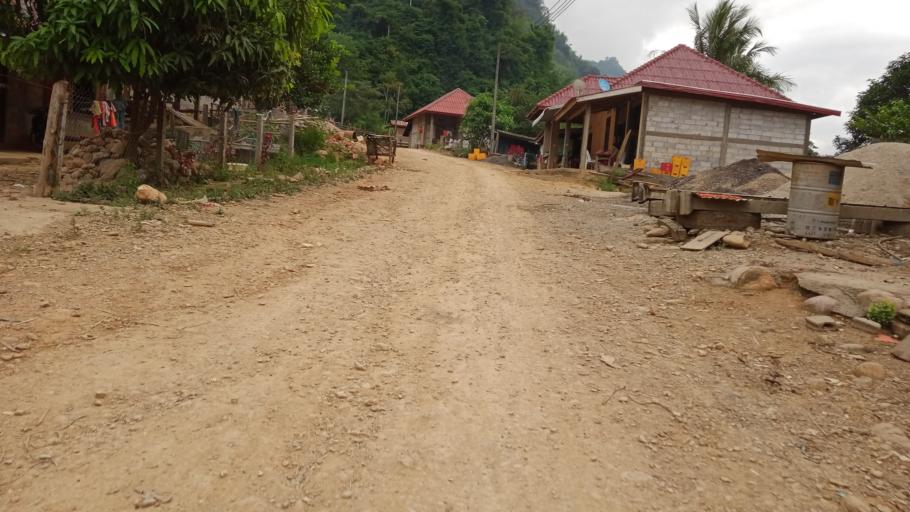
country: LA
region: Xiangkhoang
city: Phonsavan
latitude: 19.0925
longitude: 103.0031
